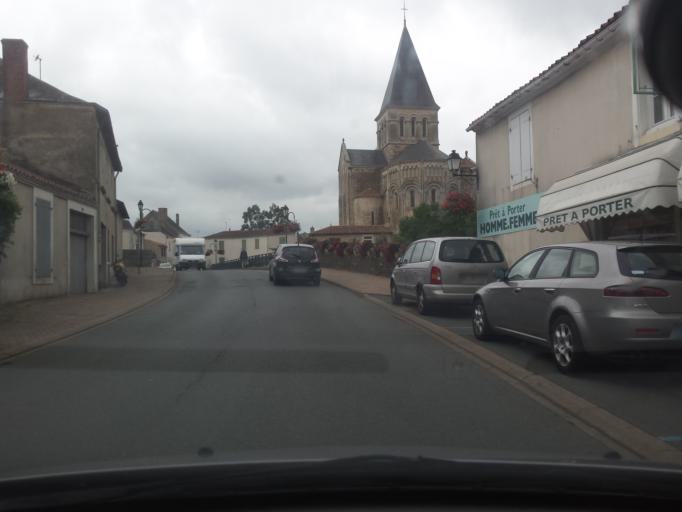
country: FR
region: Pays de la Loire
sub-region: Departement de la Vendee
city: Mareuil-sur-Lay-Dissais
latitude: 46.5350
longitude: -1.2194
